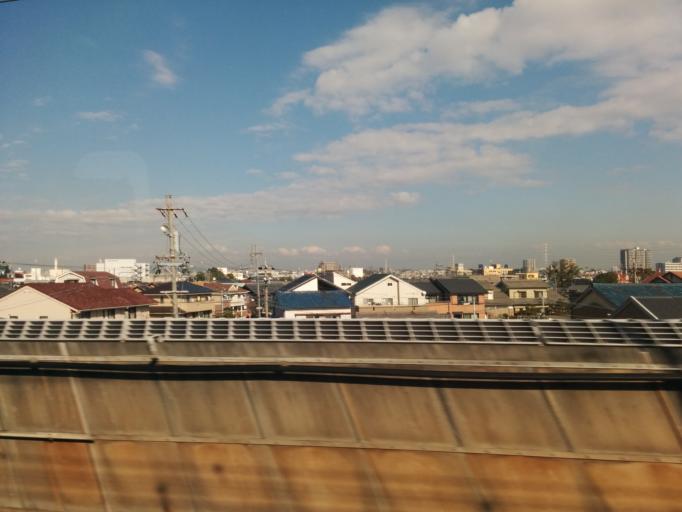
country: JP
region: Aichi
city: Obu
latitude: 35.0771
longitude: 136.9363
